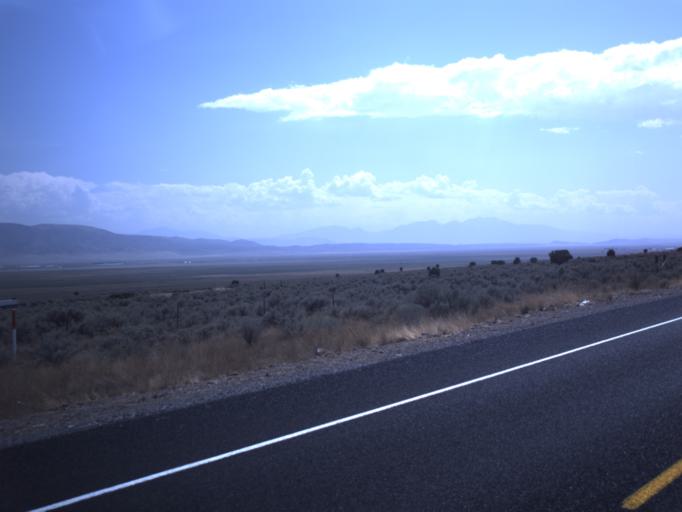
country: US
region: Utah
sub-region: Utah County
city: Eagle Mountain
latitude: 40.3198
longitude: -112.1025
